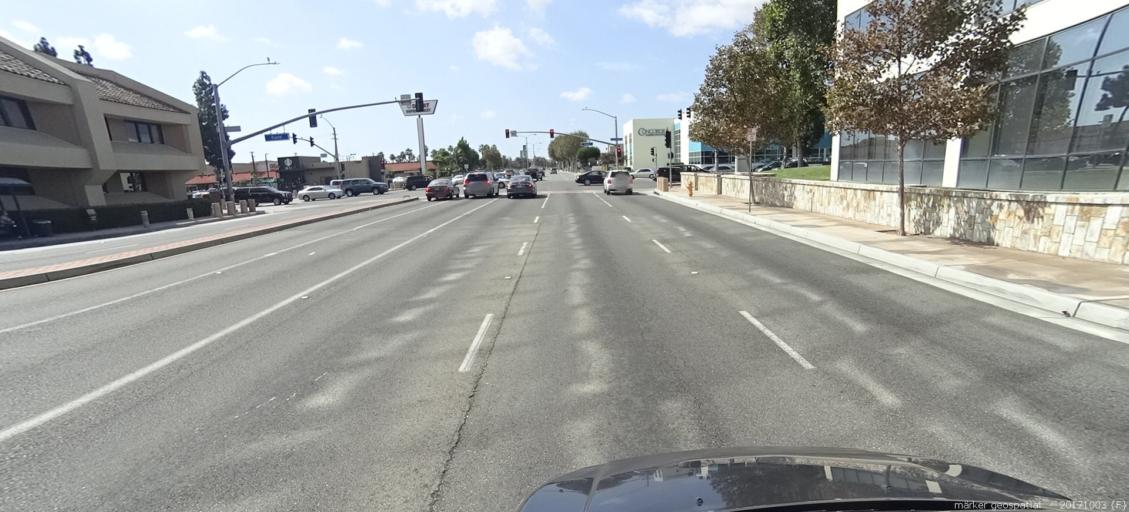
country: US
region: California
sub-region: Orange County
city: Garden Grove
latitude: 33.7743
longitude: -117.9372
